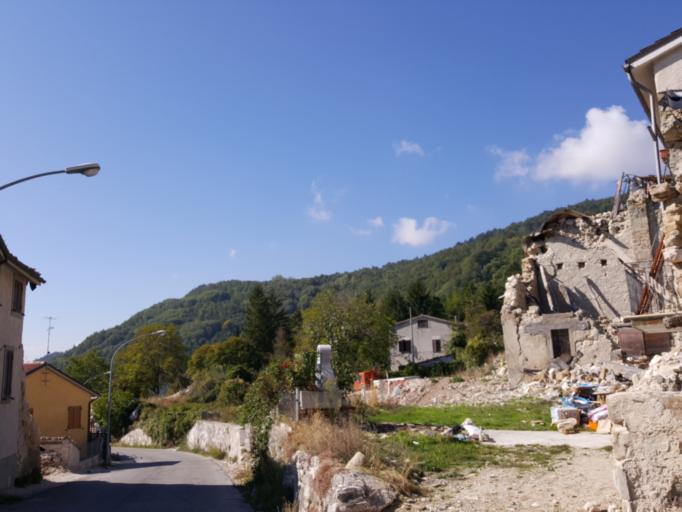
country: IT
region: The Marches
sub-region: Provincia di Ascoli Piceno
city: Arquata del Tronto
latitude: 42.7986
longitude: 13.3005
